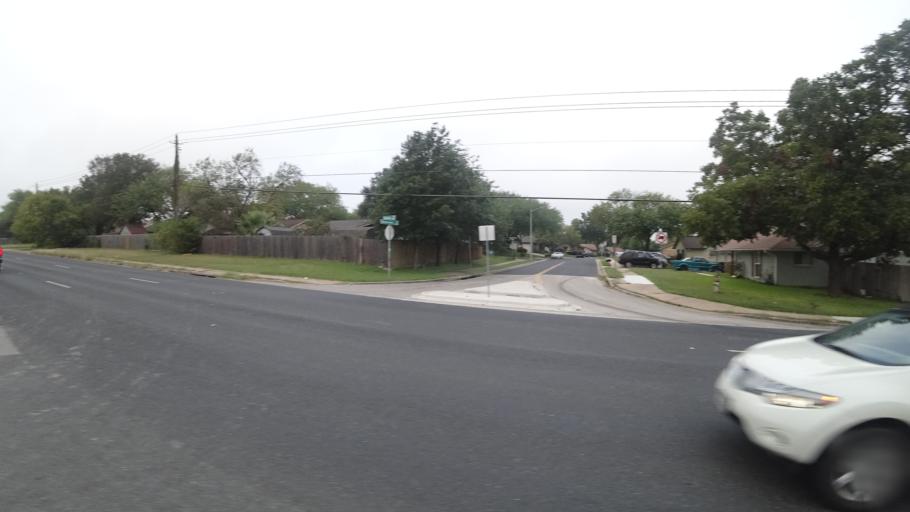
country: US
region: Texas
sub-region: Travis County
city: Wells Branch
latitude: 30.3589
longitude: -97.6708
